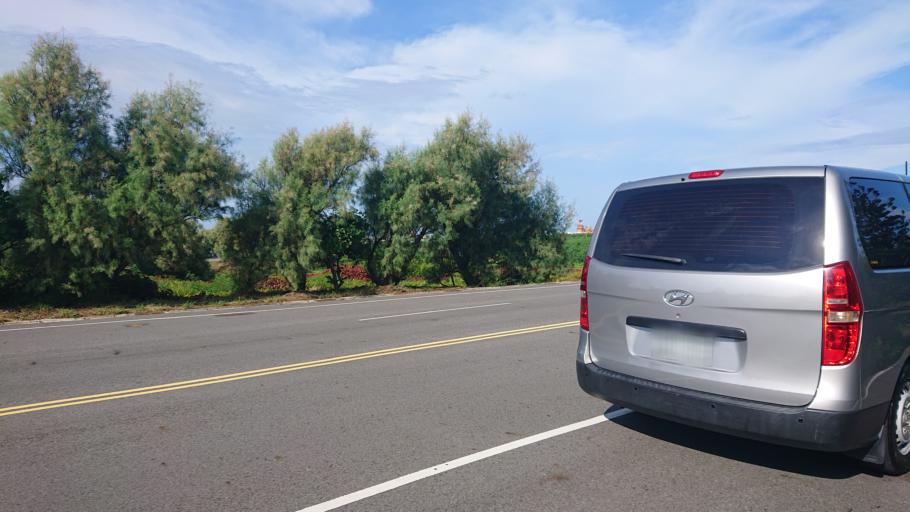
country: TW
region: Taiwan
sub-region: Penghu
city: Ma-kung
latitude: 23.5256
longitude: 119.5954
